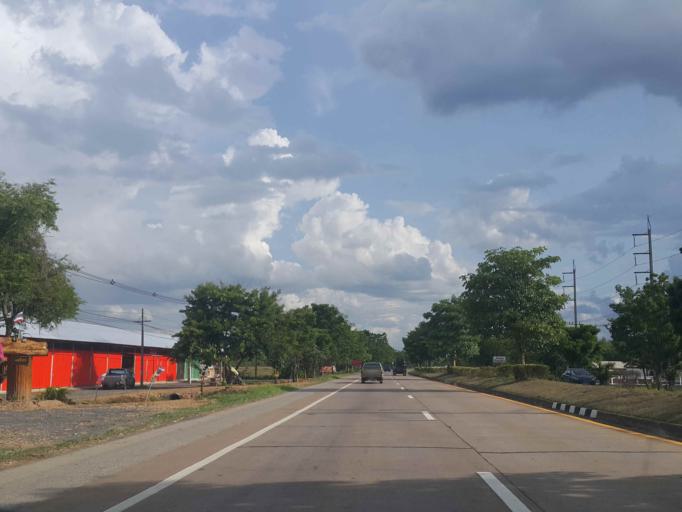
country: TH
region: Phrae
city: Sung Men
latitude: 18.0180
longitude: 100.1086
